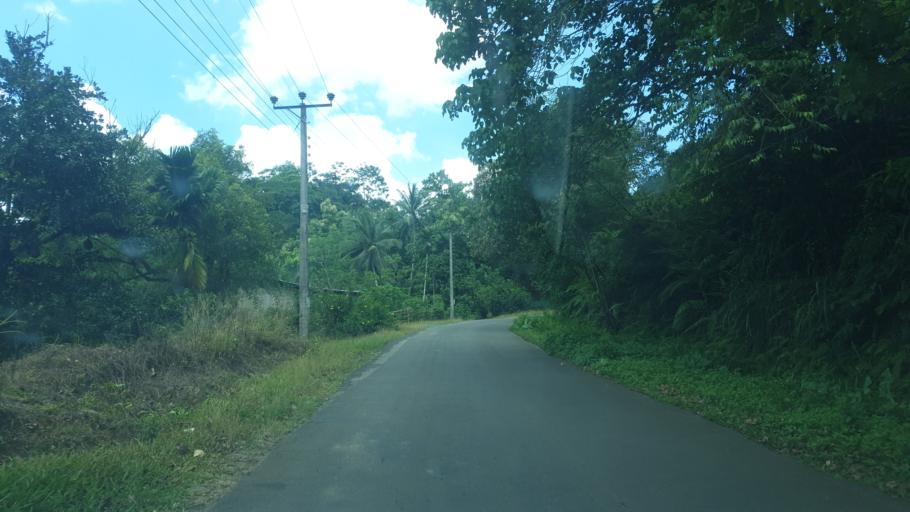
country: LK
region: Sabaragamuwa
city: Ratnapura
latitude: 6.4902
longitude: 80.3999
